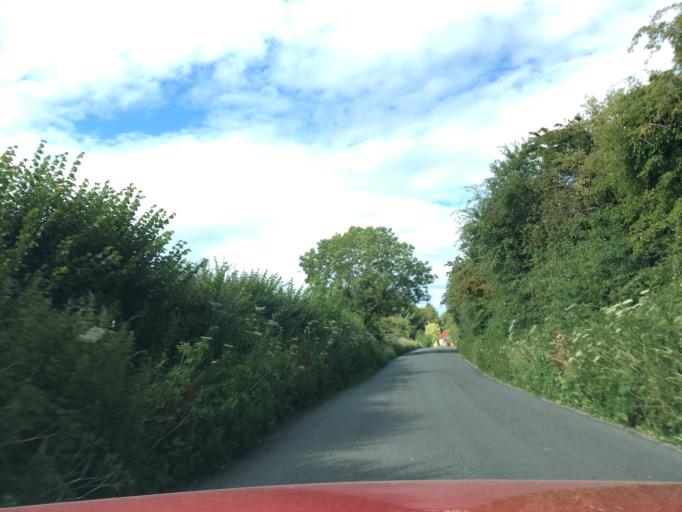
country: GB
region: England
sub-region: Gloucestershire
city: Stonehouse
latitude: 51.7847
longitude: -2.2772
